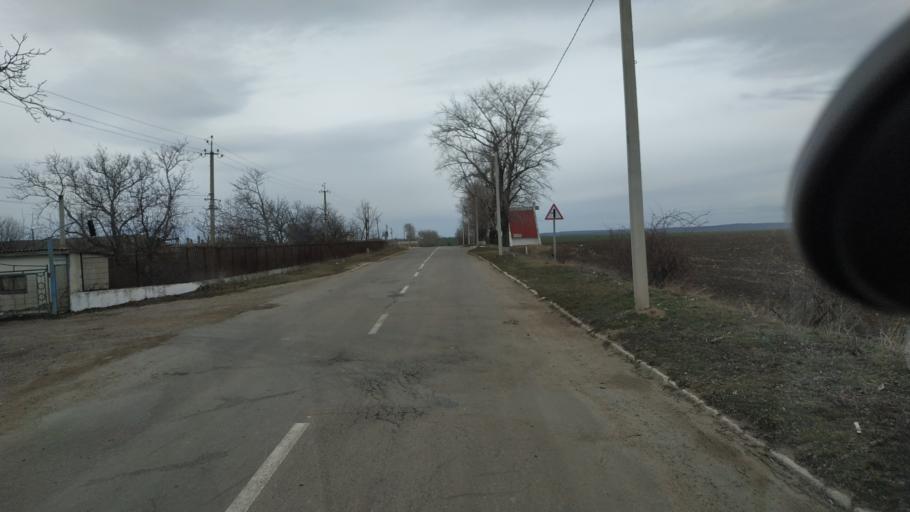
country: MD
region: Telenesti
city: Cocieri
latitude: 47.3559
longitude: 29.1164
